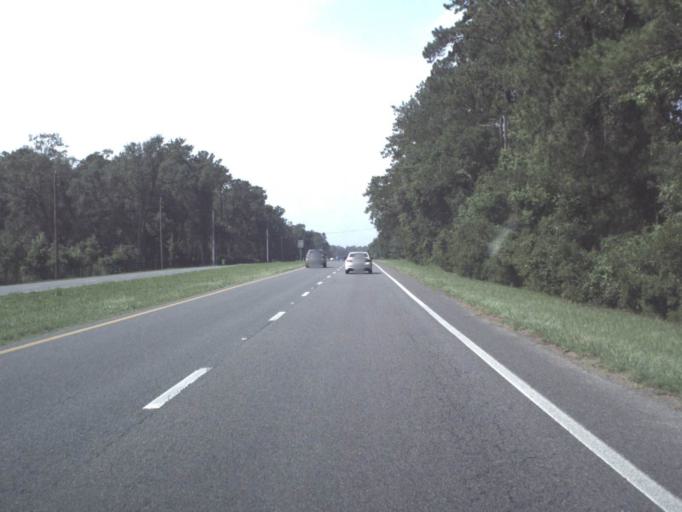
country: US
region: Florida
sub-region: Nassau County
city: Callahan
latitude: 30.5838
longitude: -81.8317
